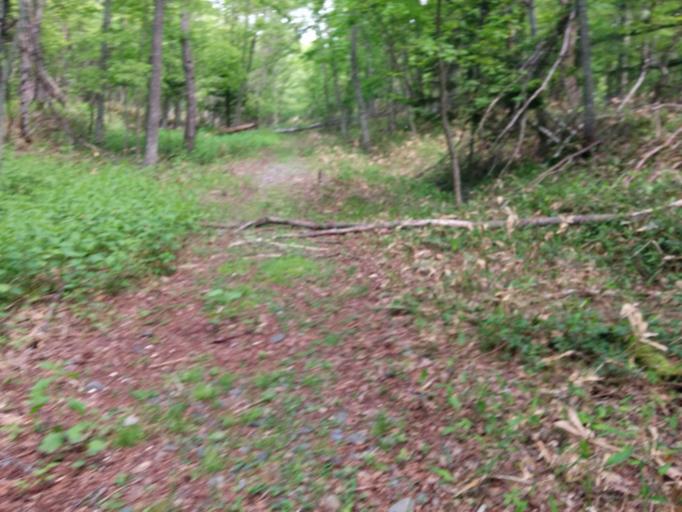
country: JP
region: Hokkaido
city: Otofuke
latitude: 43.3993
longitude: 143.1829
